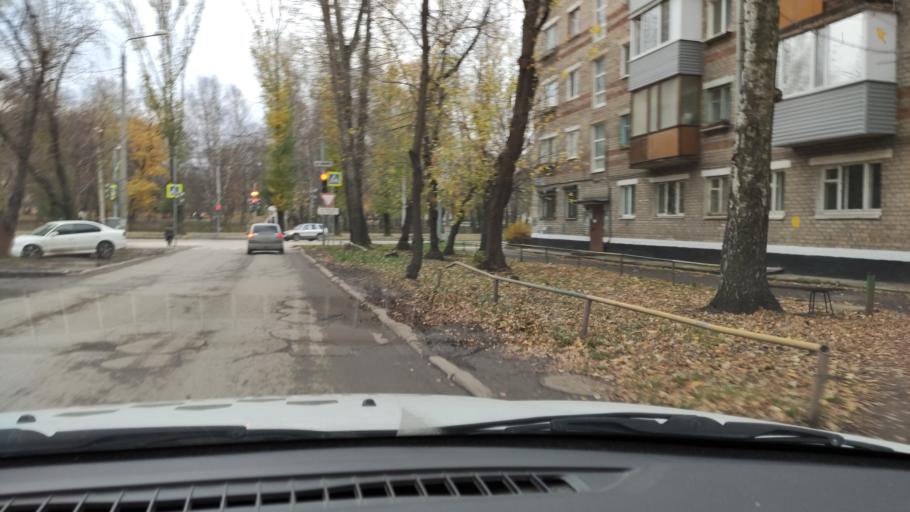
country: RU
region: Perm
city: Perm
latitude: 57.9838
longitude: 56.2031
